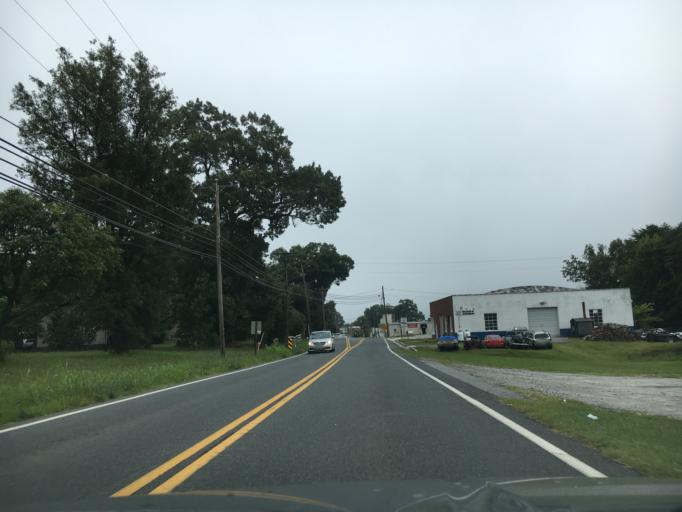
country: US
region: Virginia
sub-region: Campbell County
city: Brookneal
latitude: 37.0573
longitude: -78.9494
